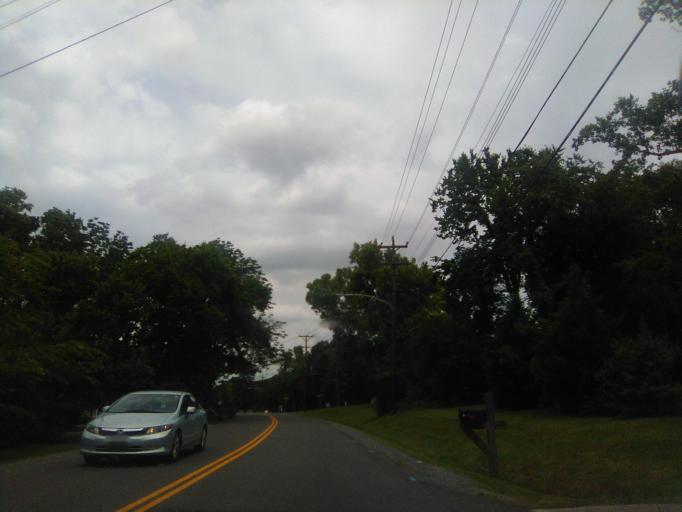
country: US
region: Tennessee
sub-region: Davidson County
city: Belle Meade
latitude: 36.1296
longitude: -86.8839
